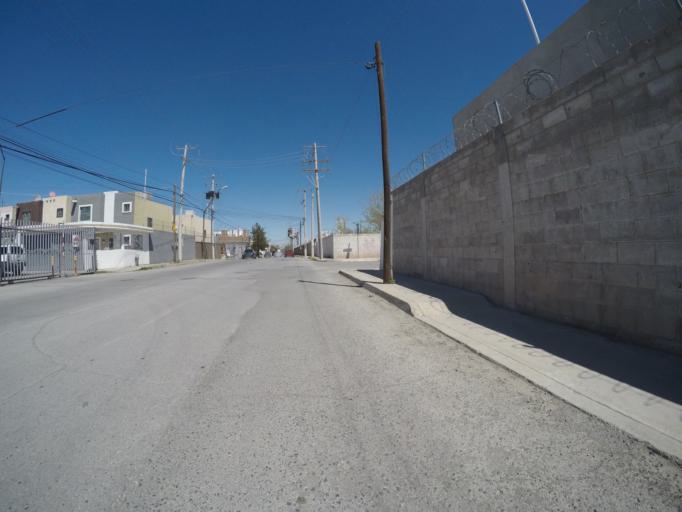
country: MX
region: Chihuahua
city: Ciudad Juarez
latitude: 31.6975
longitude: -106.4141
